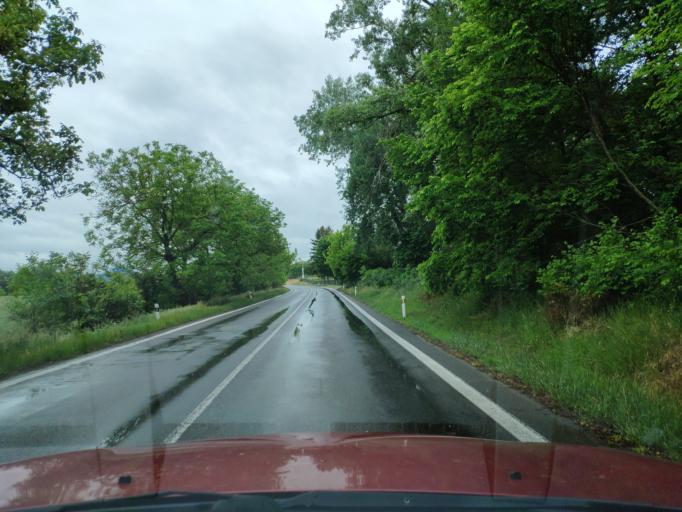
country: HU
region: Borsod-Abauj-Zemplen
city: Karcsa
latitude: 48.3911
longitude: 21.7720
